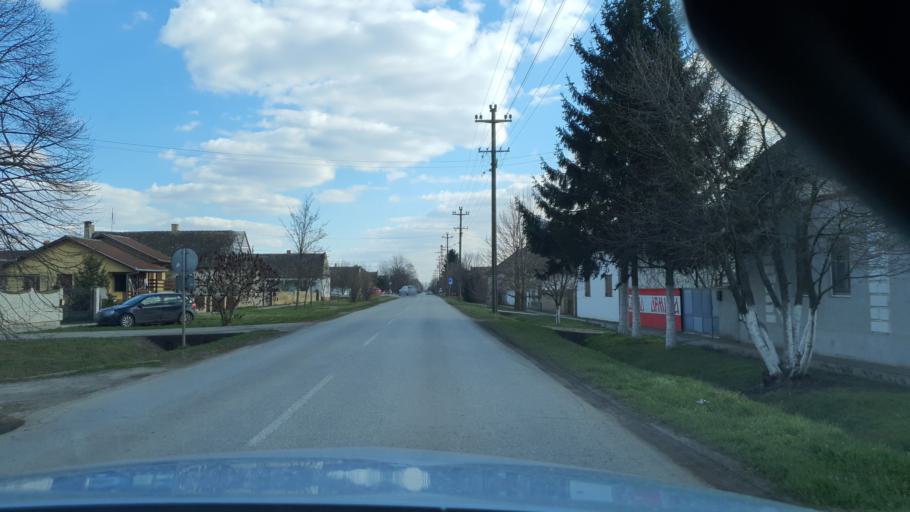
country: RS
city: Ravno Selo
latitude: 45.4479
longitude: 19.6220
